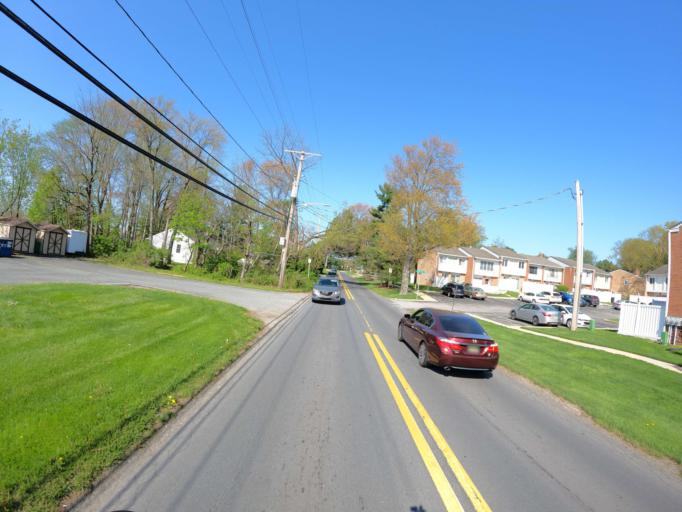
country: US
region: Delaware
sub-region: New Castle County
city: Brookside
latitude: 39.6568
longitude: -75.7498
